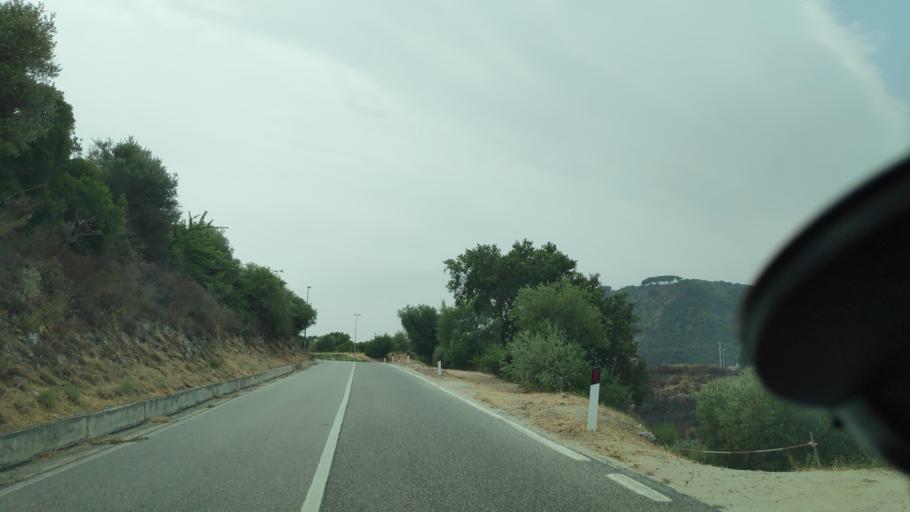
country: IT
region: Calabria
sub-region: Provincia di Catanzaro
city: Sant'Andrea Apostolo dello Ionio
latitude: 38.6430
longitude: 16.5267
